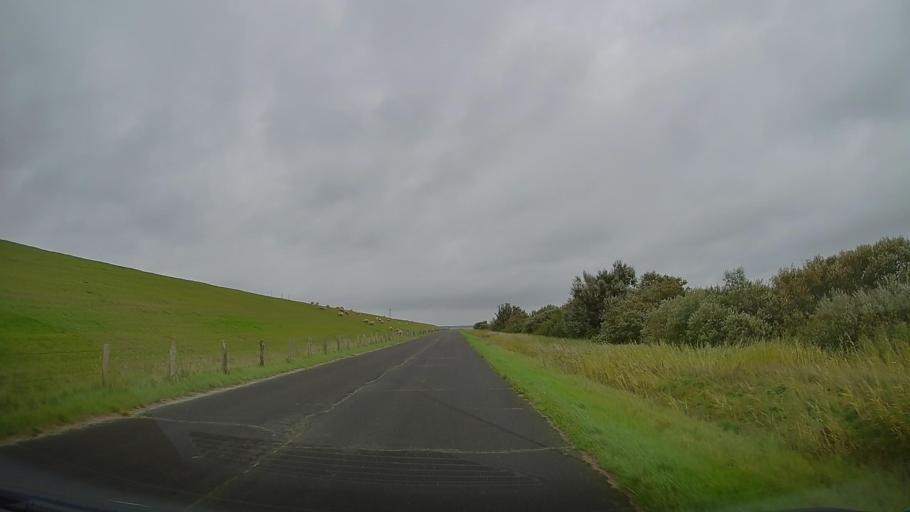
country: DE
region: Schleswig-Holstein
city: Busenwurth
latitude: 54.0492
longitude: 8.9842
